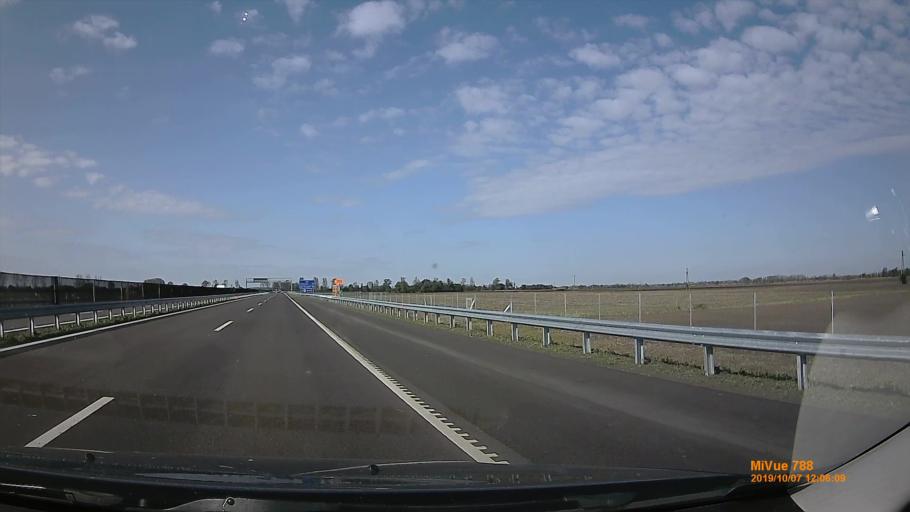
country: HU
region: Bekes
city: Bekesszentandras
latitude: 46.8213
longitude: 20.5048
